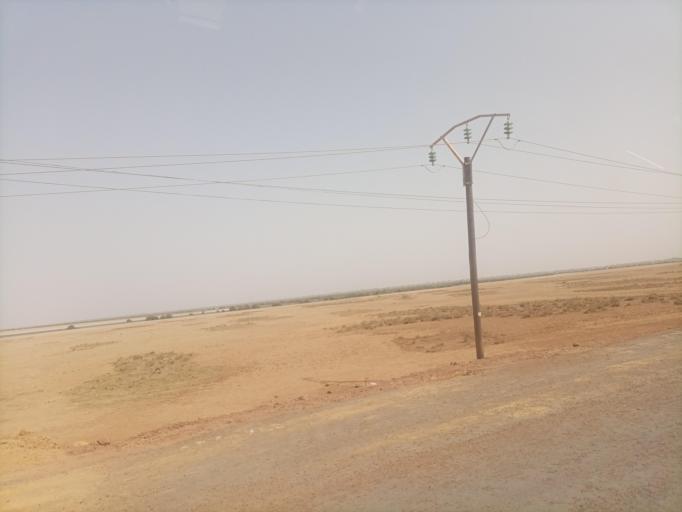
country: SN
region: Fatick
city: Foundiougne
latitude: 14.1515
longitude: -16.4707
